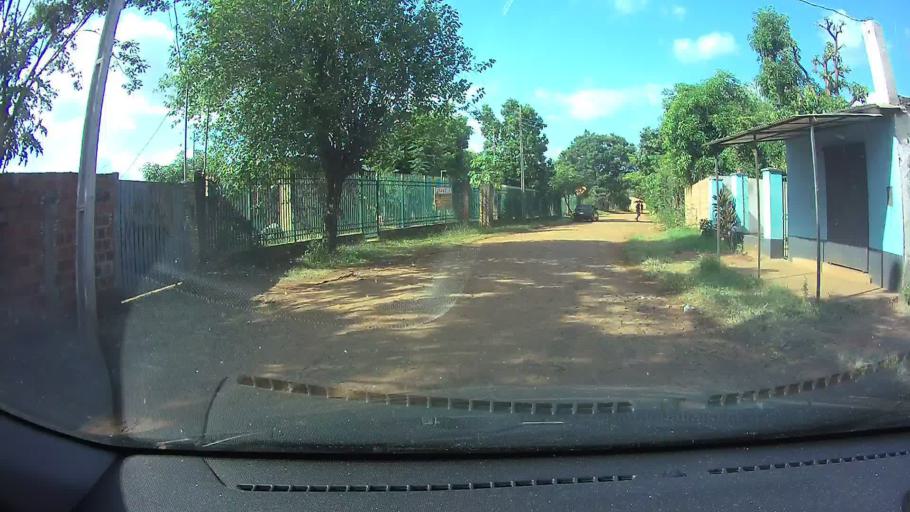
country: PY
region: Central
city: Limpio
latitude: -25.2425
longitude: -57.4669
